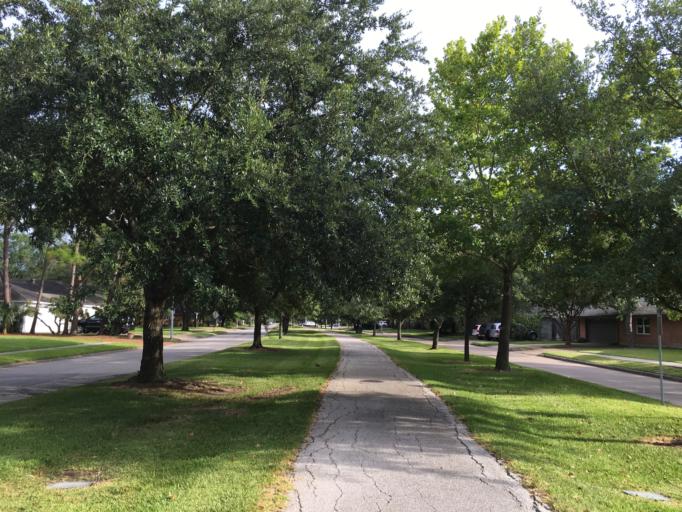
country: US
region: Texas
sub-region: Harris County
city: Piney Point Village
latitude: 29.7321
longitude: -95.5064
